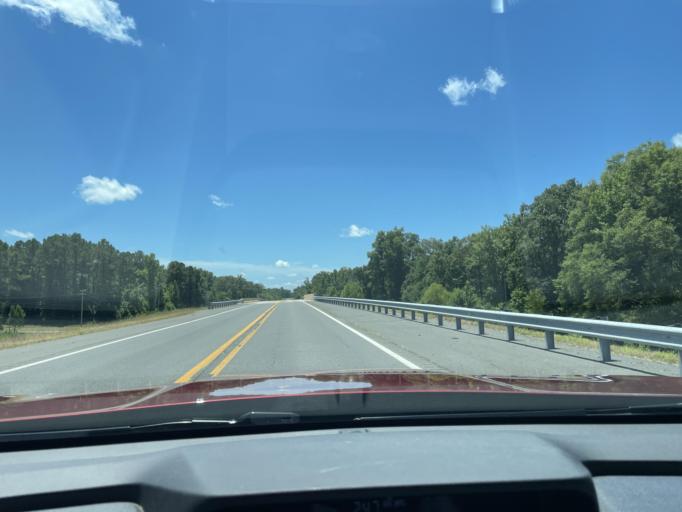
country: US
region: Arkansas
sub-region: Jefferson County
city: Pine Bluff
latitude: 34.1304
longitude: -91.9715
